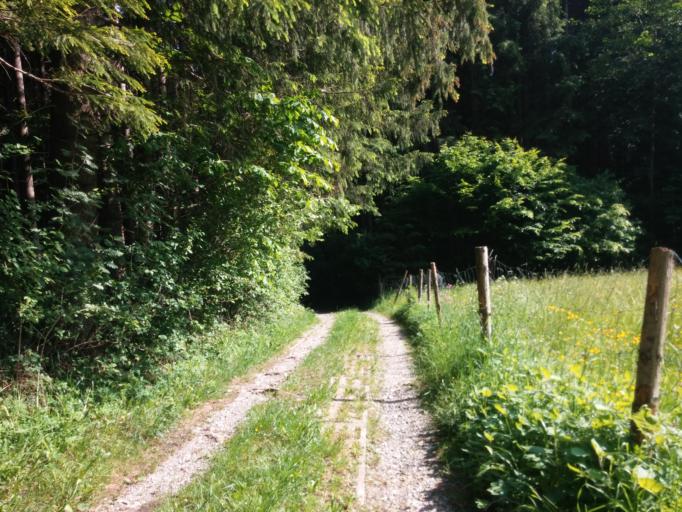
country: DE
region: Bavaria
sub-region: Swabia
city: Woringen
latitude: 47.8767
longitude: 10.1999
